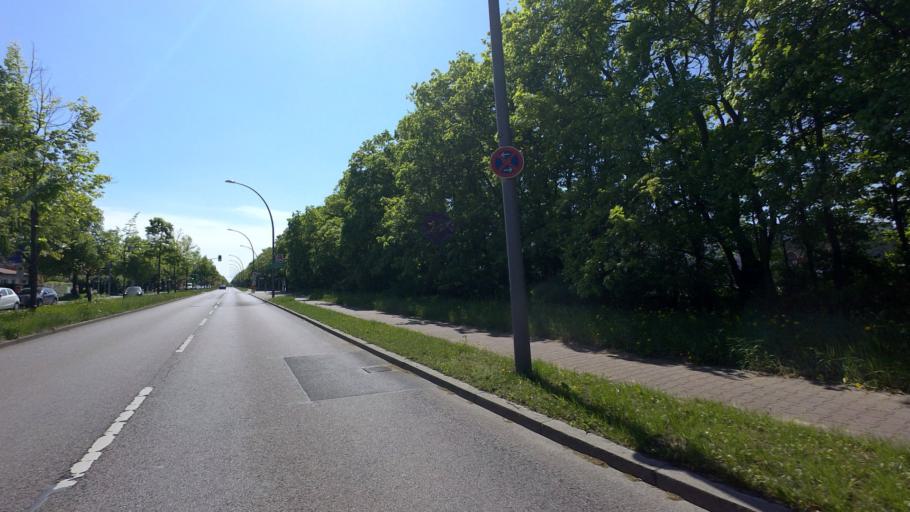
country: DE
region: Brandenburg
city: Schonefeld
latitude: 52.4052
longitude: 13.5097
